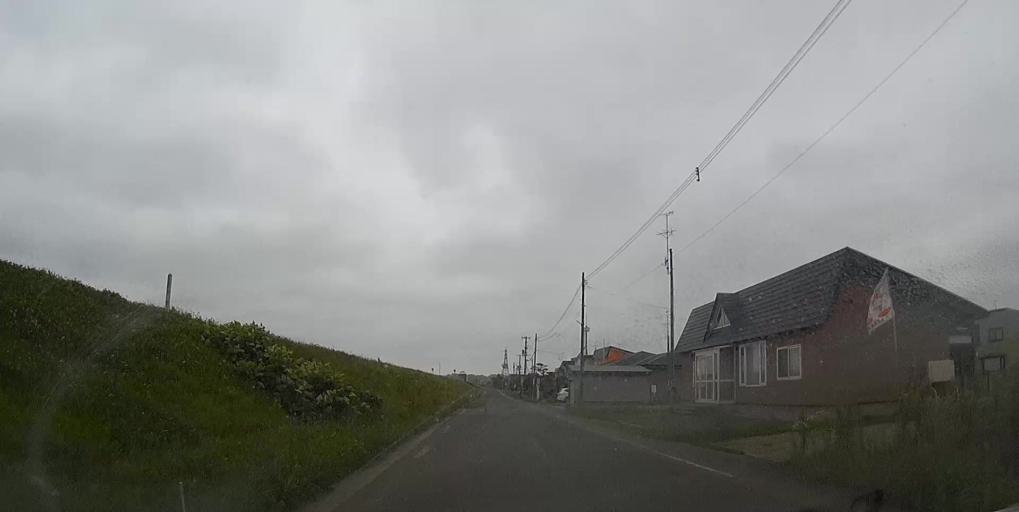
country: JP
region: Hokkaido
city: Iwanai
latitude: 42.4226
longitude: 140.0145
